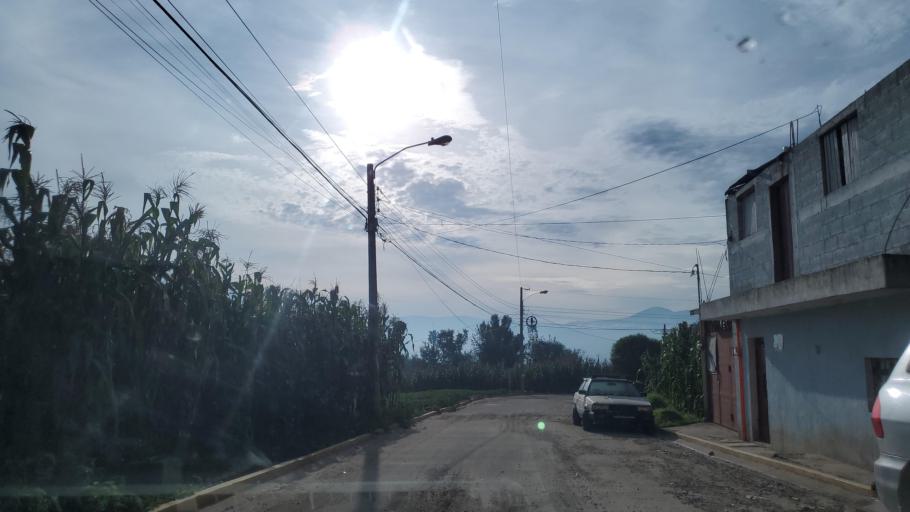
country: GT
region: Quetzaltenango
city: Quetzaltenango
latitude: 14.8425
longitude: -91.5471
